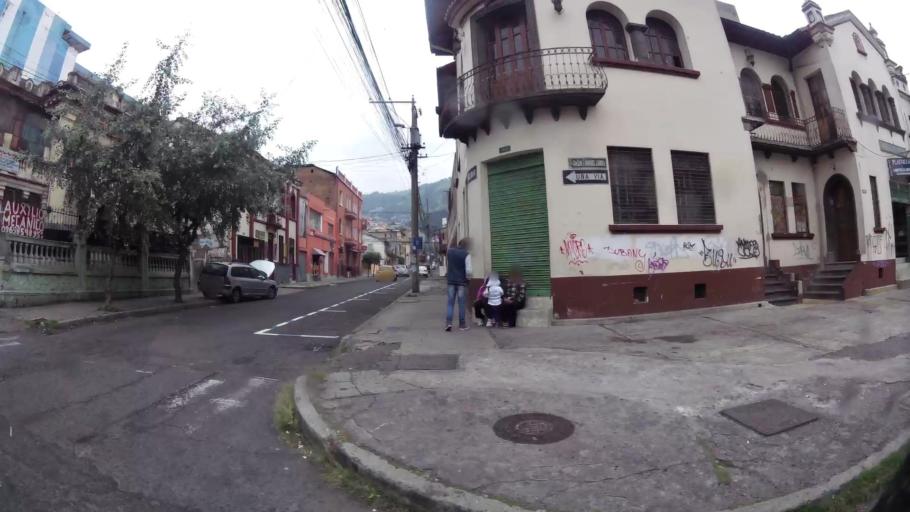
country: EC
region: Pichincha
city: Quito
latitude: -0.2101
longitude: -78.5023
